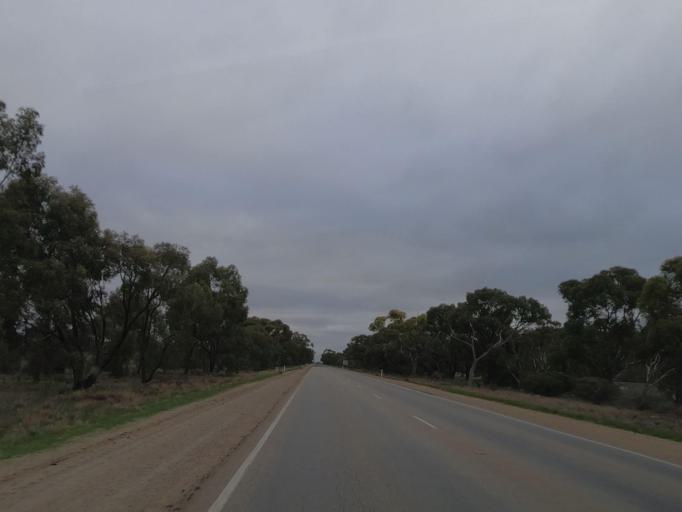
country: AU
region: Victoria
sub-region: Swan Hill
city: Swan Hill
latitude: -35.4030
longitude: 143.5789
